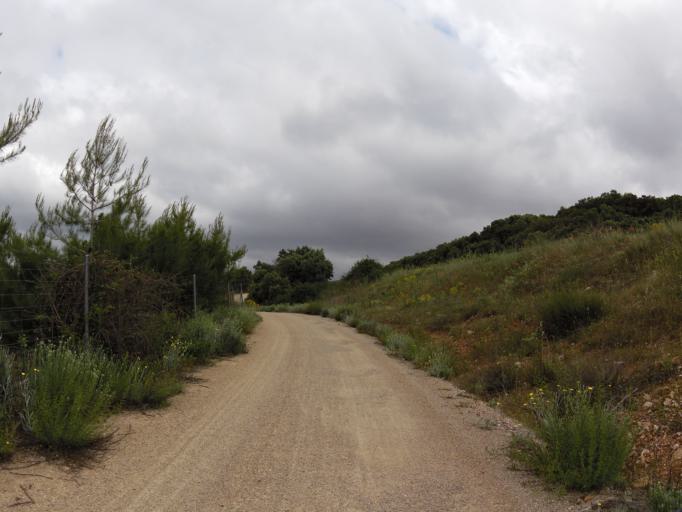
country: ES
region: Castille-La Mancha
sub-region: Provincia de Albacete
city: Robledo
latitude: 38.7333
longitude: -2.4668
